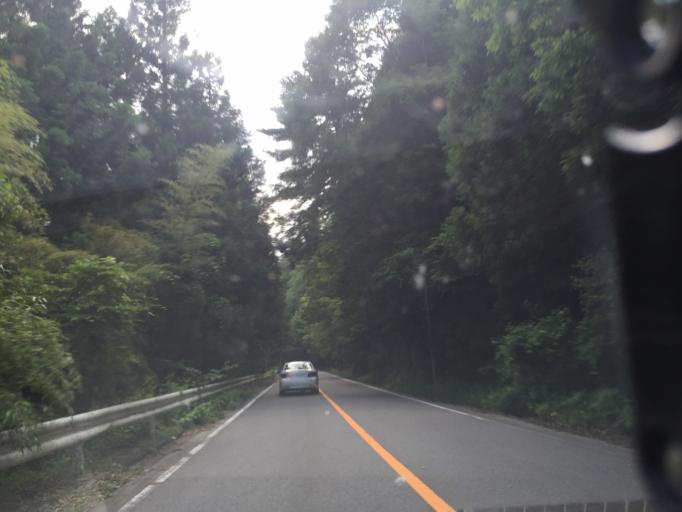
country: JP
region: Aichi
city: Shinshiro
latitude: 35.1839
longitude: 137.6152
